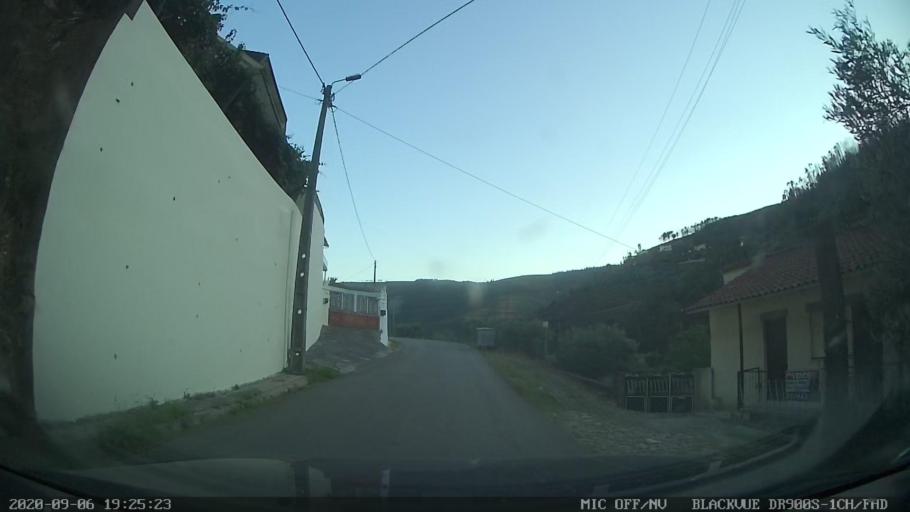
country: PT
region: Vila Real
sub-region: Mesao Frio
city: Mesao Frio
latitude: 41.1875
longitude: -7.9212
